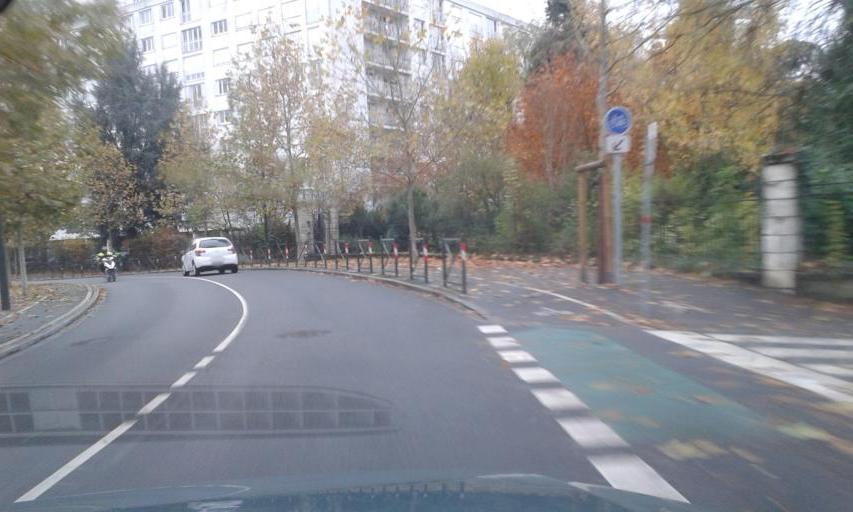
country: FR
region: Centre
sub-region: Departement du Loiret
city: Olivet
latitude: 47.8738
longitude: 1.9048
